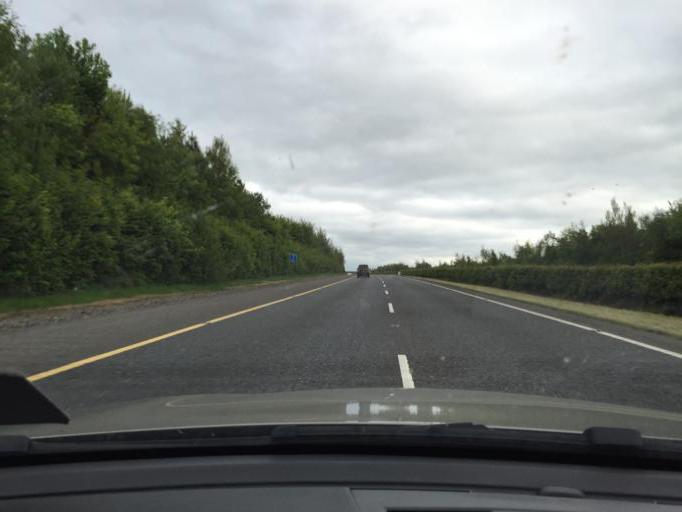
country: IE
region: Leinster
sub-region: An Mhi
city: Stamullin
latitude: 53.6225
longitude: -6.2473
